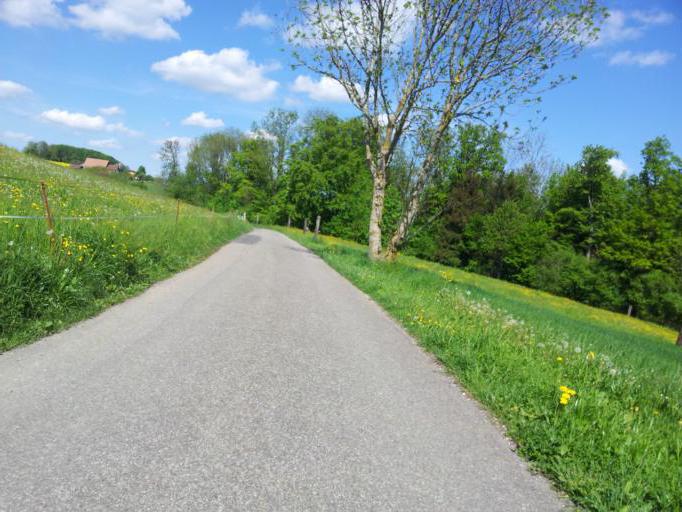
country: CH
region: Aargau
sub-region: Bezirk Bremgarten
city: Rudolfstetten
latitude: 47.3749
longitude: 8.3655
